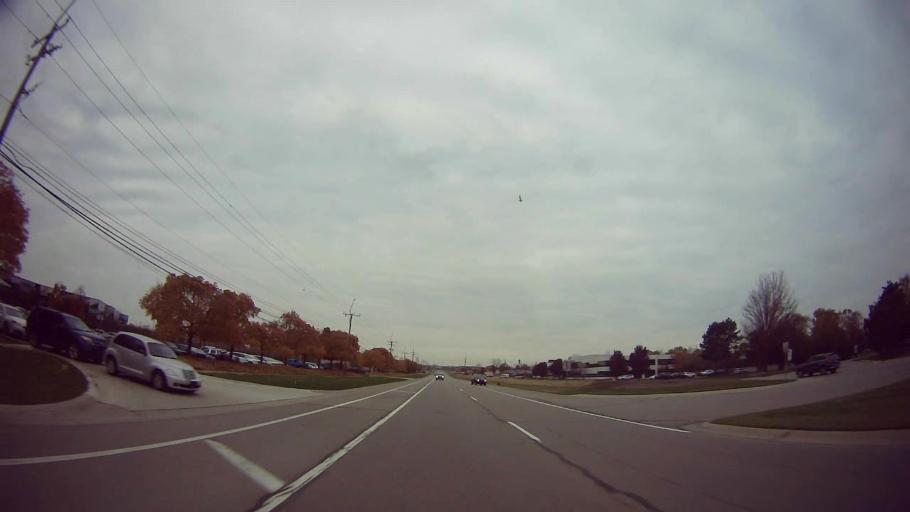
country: US
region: Michigan
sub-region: Oakland County
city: Franklin
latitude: 42.5232
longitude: -83.3475
